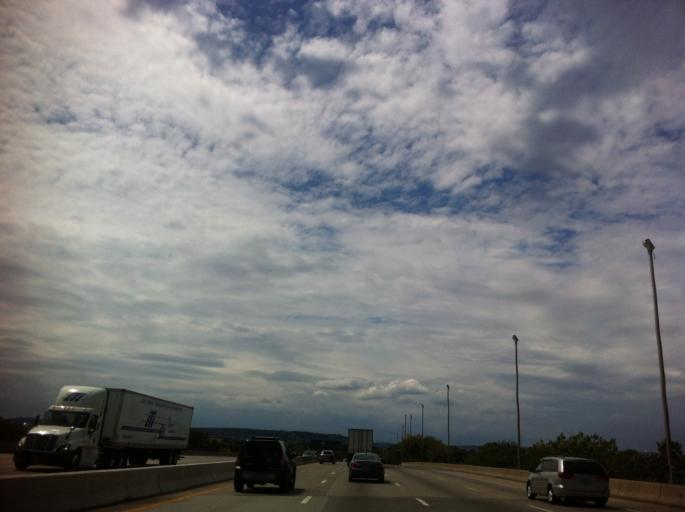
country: US
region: New Jersey
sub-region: Bergen County
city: Saddle Brook
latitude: 40.9034
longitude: -74.0967
